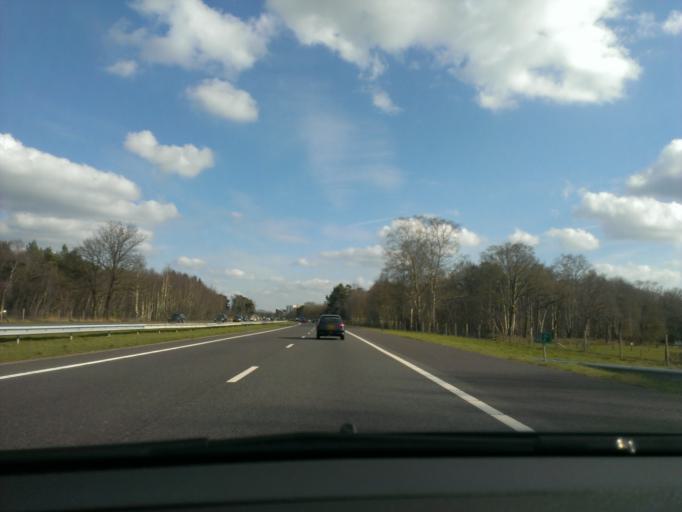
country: NL
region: Overijssel
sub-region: Gemeente Hengelo
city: Hengelo
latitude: 52.2144
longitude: 6.8048
